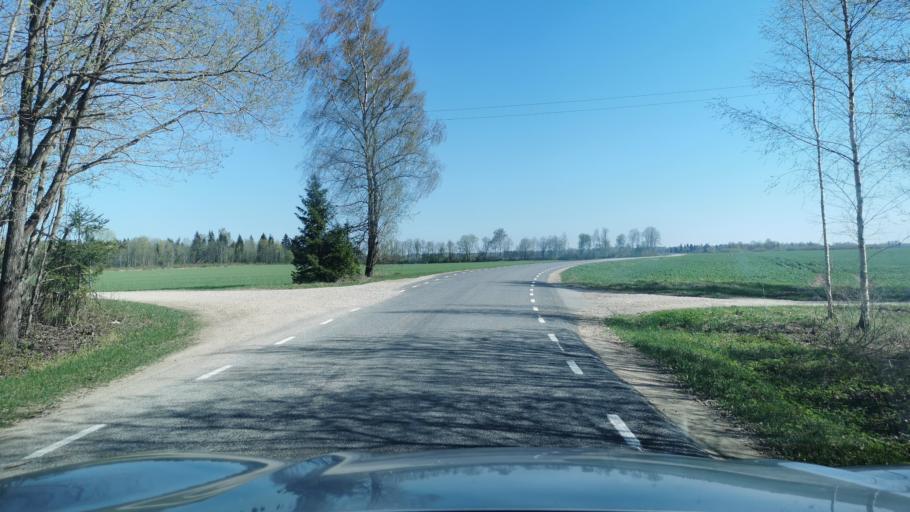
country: EE
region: Laeaene-Virumaa
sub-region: Vinni vald
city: Vinni
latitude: 59.0821
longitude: 26.5905
